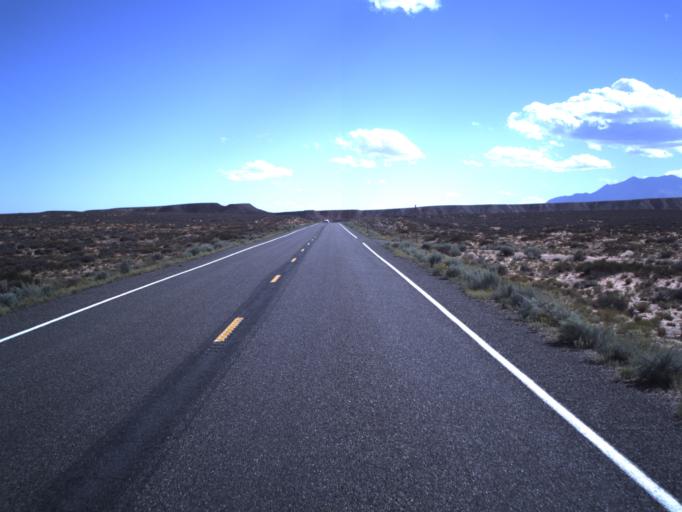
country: US
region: Utah
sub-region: Wayne County
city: Loa
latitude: 38.1678
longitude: -110.6235
